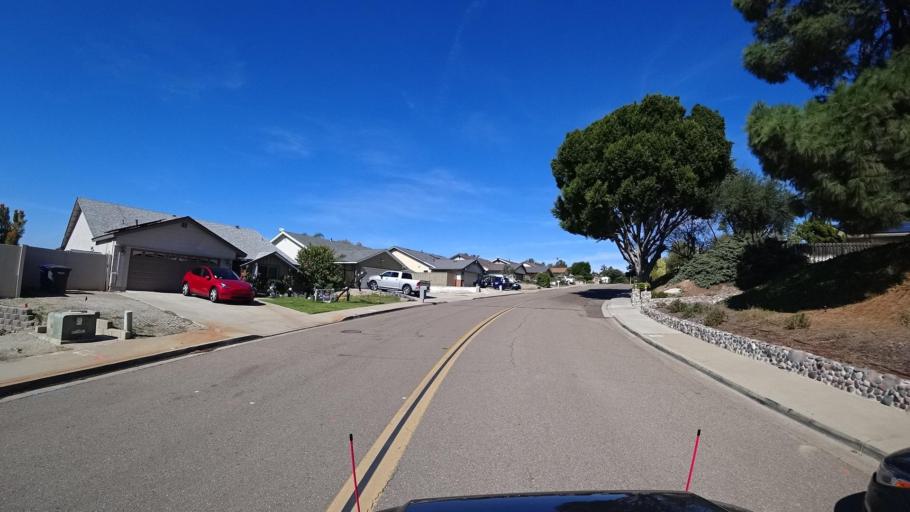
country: US
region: California
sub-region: San Diego County
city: Casa de Oro-Mount Helix
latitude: 32.7503
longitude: -116.9727
